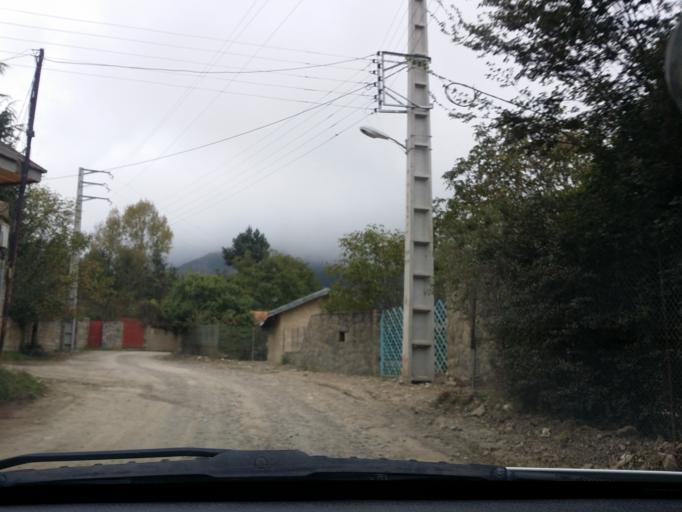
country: IR
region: Mazandaran
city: `Abbasabad
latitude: 36.4905
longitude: 51.1422
